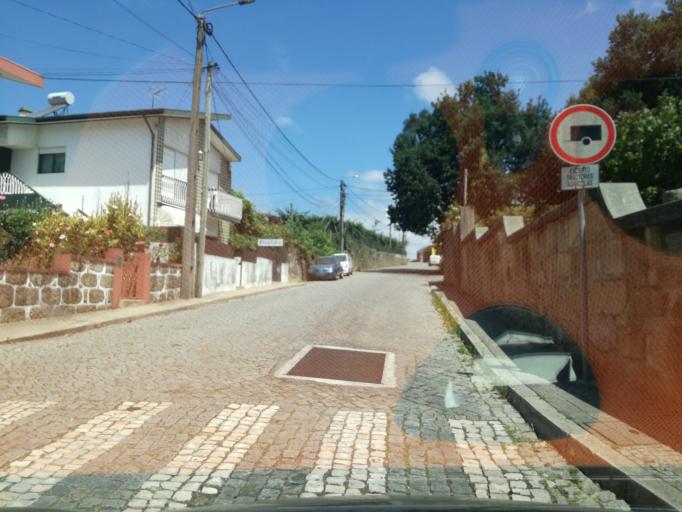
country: PT
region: Porto
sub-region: Maia
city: Maia
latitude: 41.2427
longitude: -8.6084
